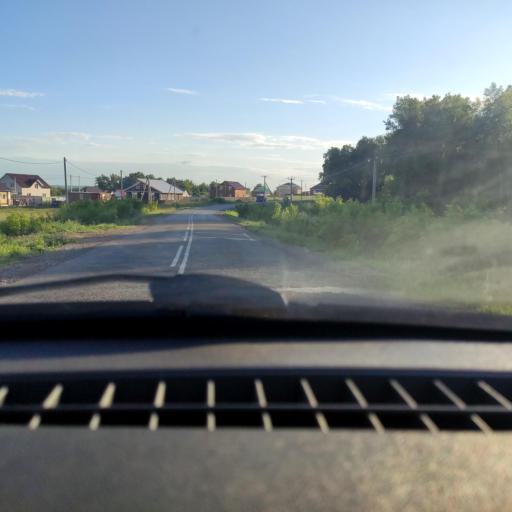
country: RU
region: Bashkortostan
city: Avdon
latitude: 54.6201
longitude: 55.6722
